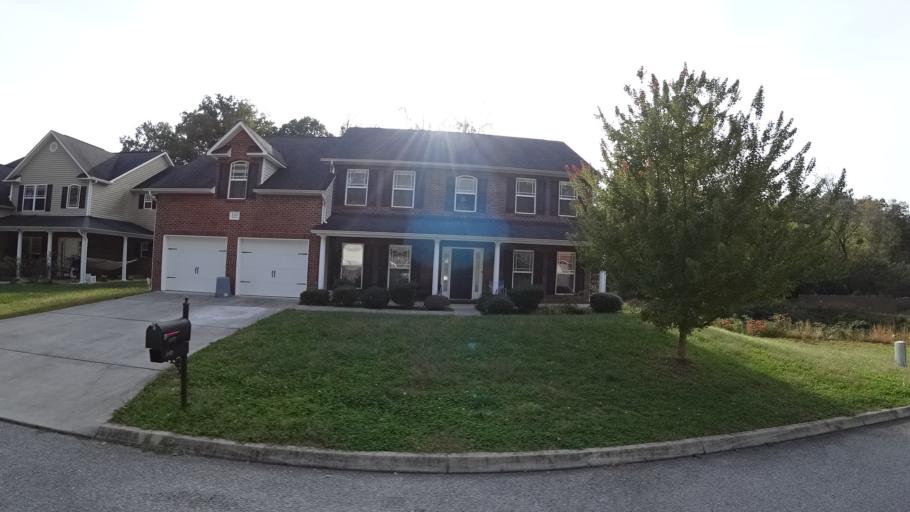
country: US
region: Tennessee
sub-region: Knox County
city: Farragut
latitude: 35.9121
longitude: -84.1625
